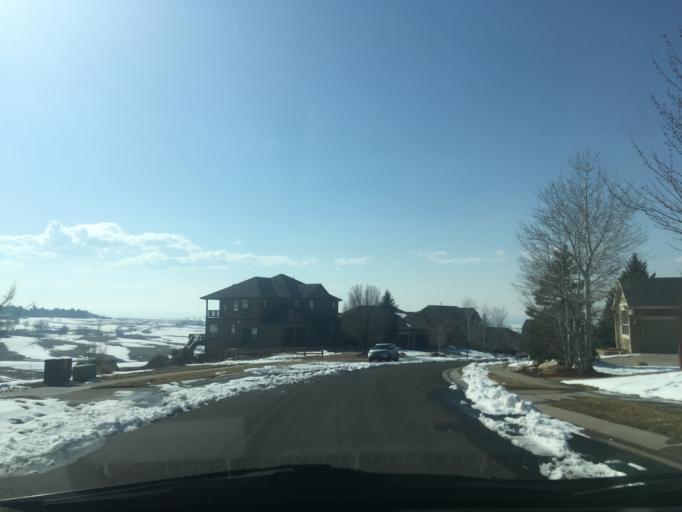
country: US
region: Colorado
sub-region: Boulder County
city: Lafayette
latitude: 39.9661
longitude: -105.0497
